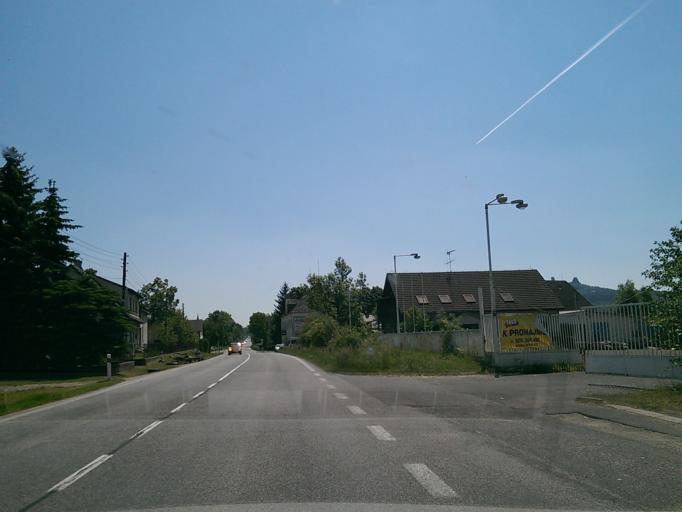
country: CZ
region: Liberecky
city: Rovensko pod Troskami
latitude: 50.5447
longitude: 15.2212
